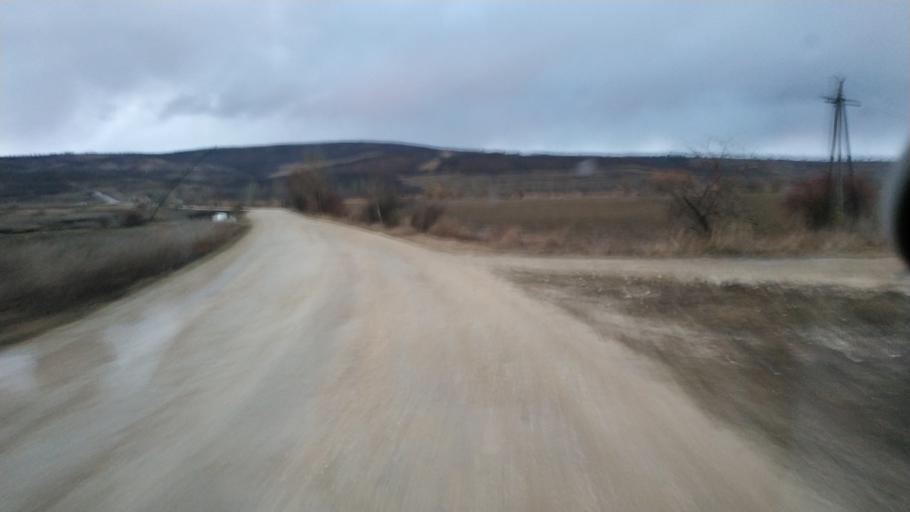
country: MD
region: Taraclia
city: Telenesti
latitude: 47.3894
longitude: 28.3317
